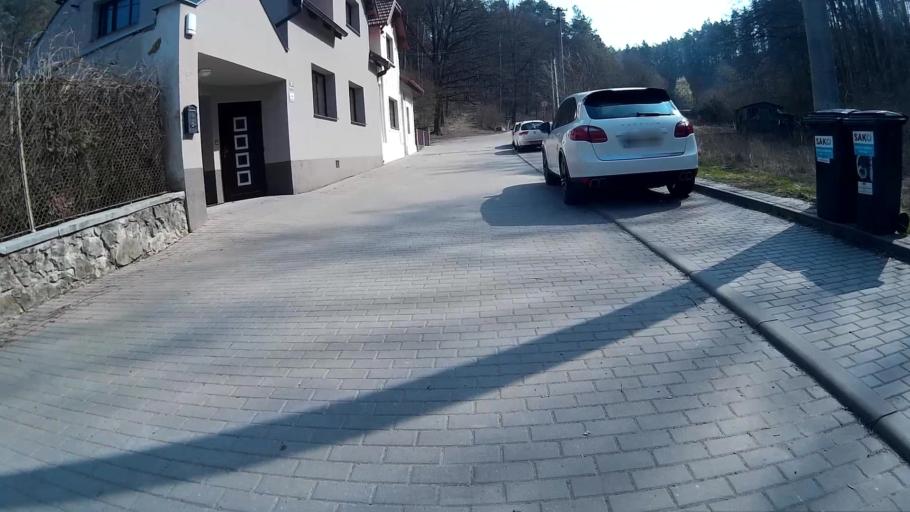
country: CZ
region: South Moravian
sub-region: Mesto Brno
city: Mokra Hora
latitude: 49.2575
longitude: 16.5958
